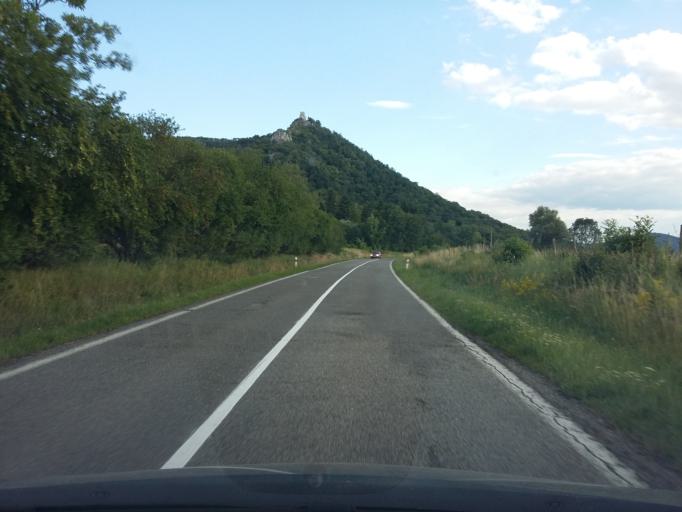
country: SK
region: Trnavsky
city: Smolenice
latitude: 48.5024
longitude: 17.2669
